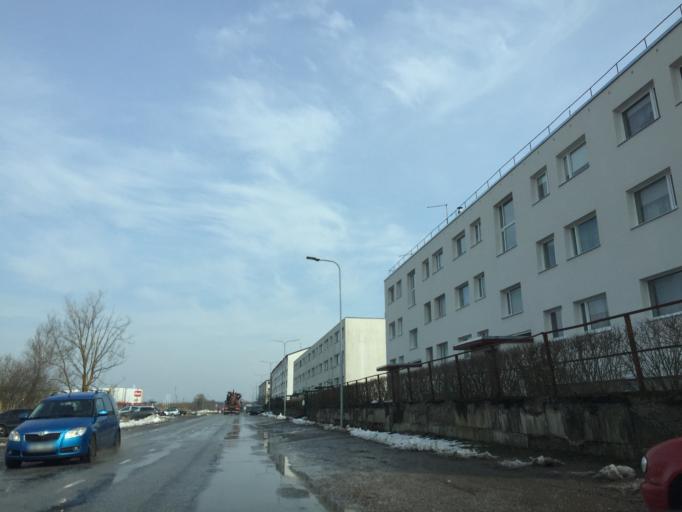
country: EE
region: Saare
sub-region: Kuressaare linn
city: Kuressaare
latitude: 58.2605
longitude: 22.4803
